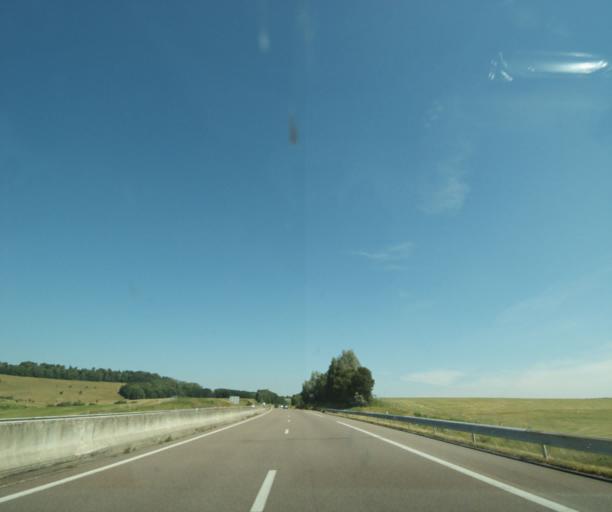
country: FR
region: Lorraine
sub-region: Departement des Vosges
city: Chatenois
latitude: 48.3839
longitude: 5.8819
